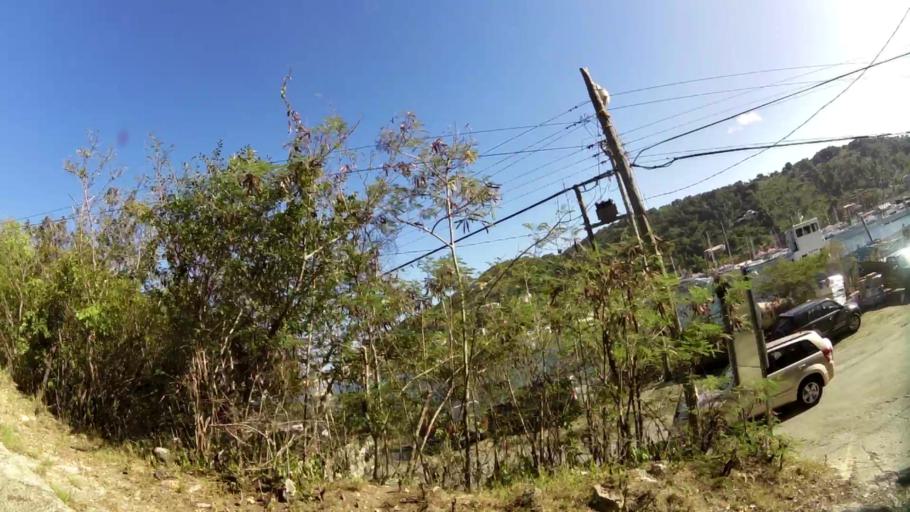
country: VG
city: Road Town
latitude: 18.3883
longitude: -64.7025
